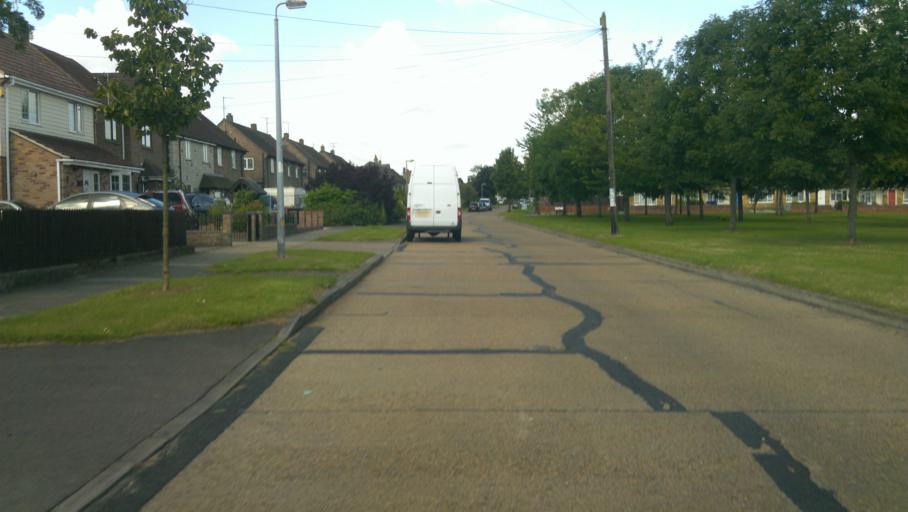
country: GB
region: England
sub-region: Essex
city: Colchester
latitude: 51.8748
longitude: 0.9156
